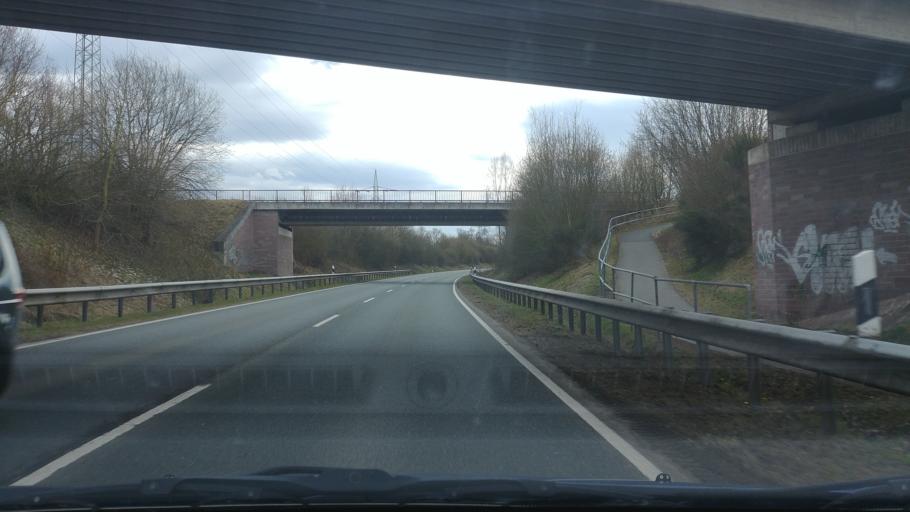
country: DE
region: Lower Saxony
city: Bevern
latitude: 51.8312
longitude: 9.4824
